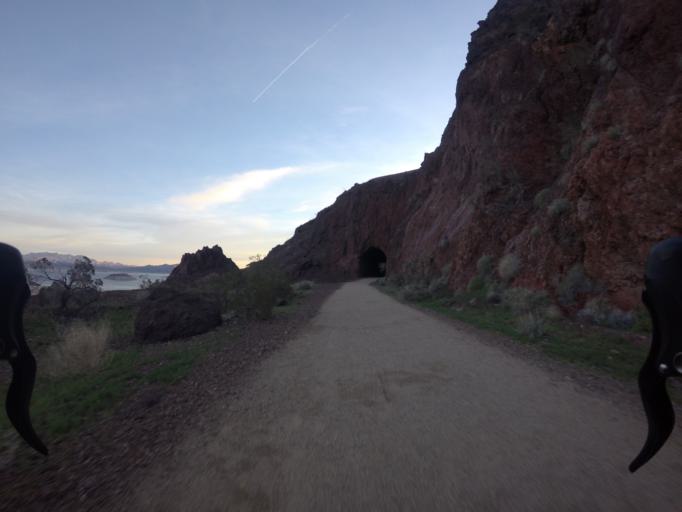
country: US
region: Nevada
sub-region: Clark County
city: Boulder City
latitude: 36.0167
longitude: -114.7632
